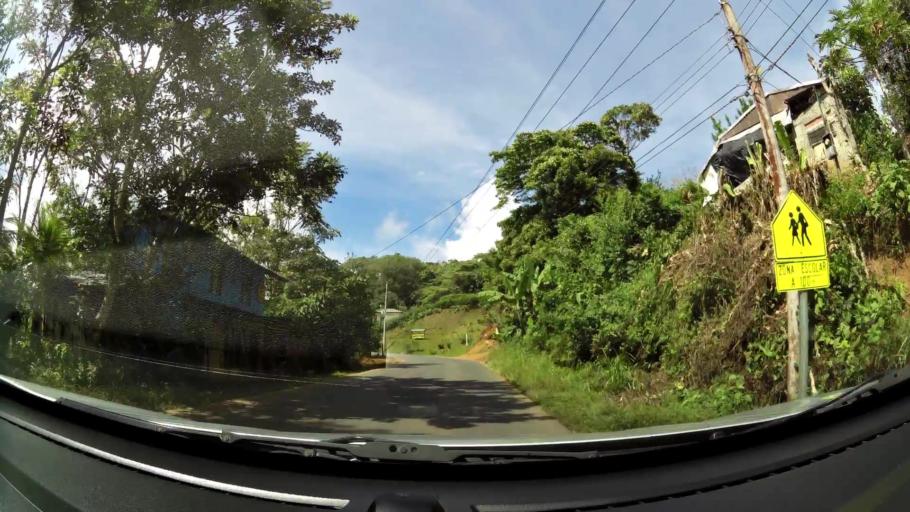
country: CR
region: San Jose
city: San Isidro
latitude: 9.3264
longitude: -83.7434
